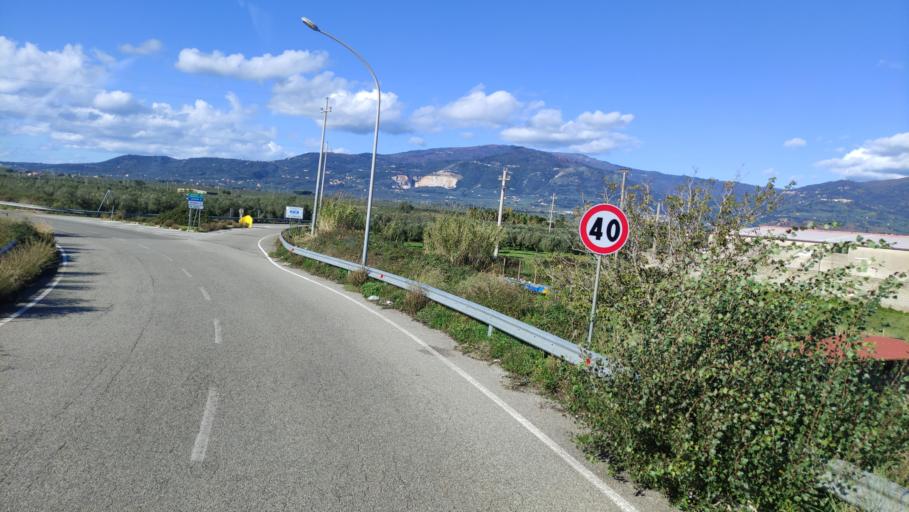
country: IT
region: Calabria
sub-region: Provincia di Catanzaro
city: Santa Eufemia Lamezia
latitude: 38.9206
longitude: 16.2742
